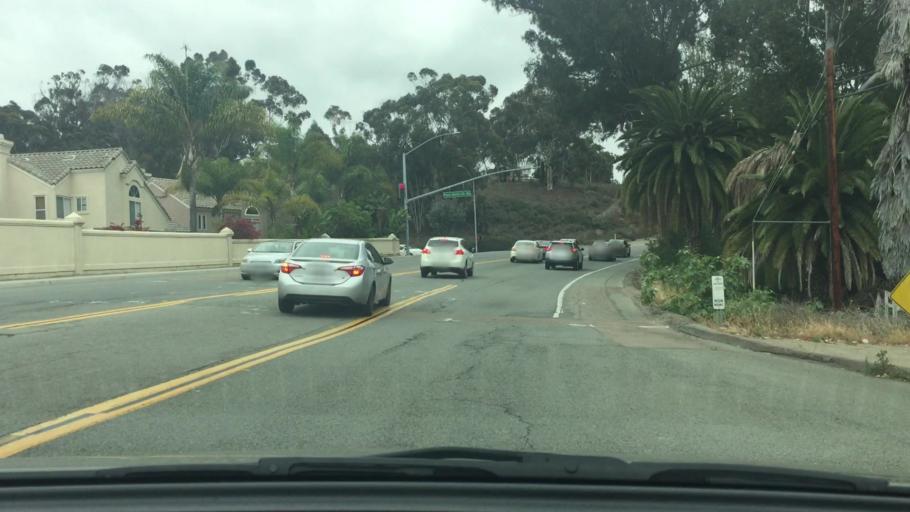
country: US
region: California
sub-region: San Diego County
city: Bonita
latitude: 32.6594
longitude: -117.0564
